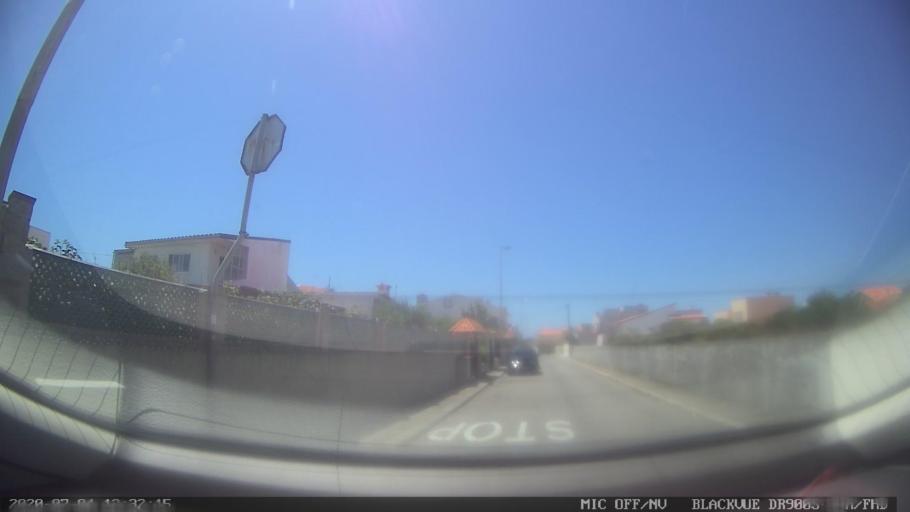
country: PT
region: Porto
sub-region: Matosinhos
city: Lavra
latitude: 41.2525
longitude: -8.7200
